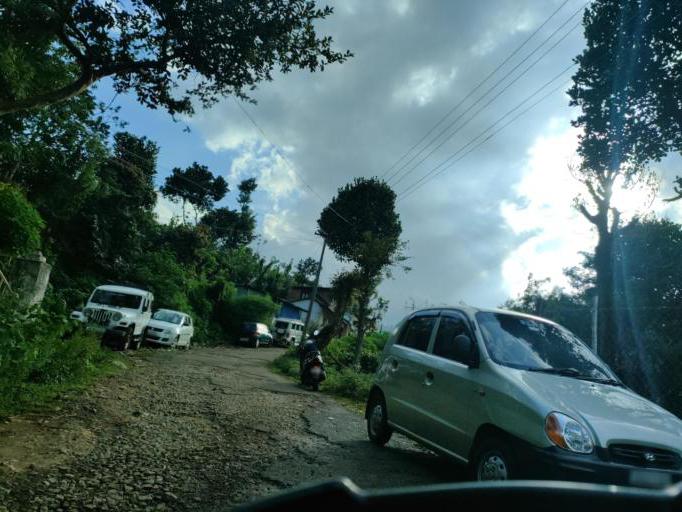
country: IN
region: Tamil Nadu
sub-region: Dindigul
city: Kodaikanal
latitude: 10.2837
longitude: 77.5312
